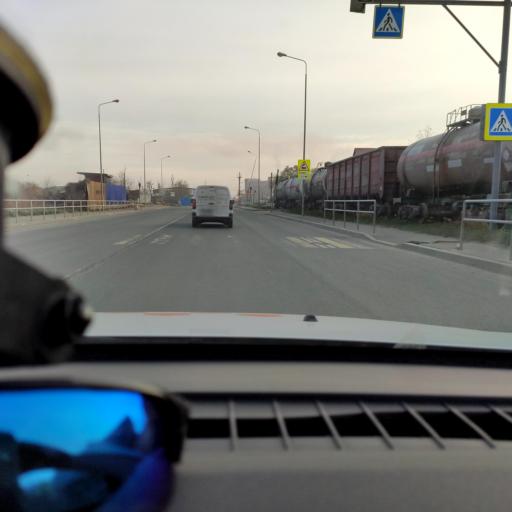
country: RU
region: Samara
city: Samara
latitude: 53.1810
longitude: 50.2106
